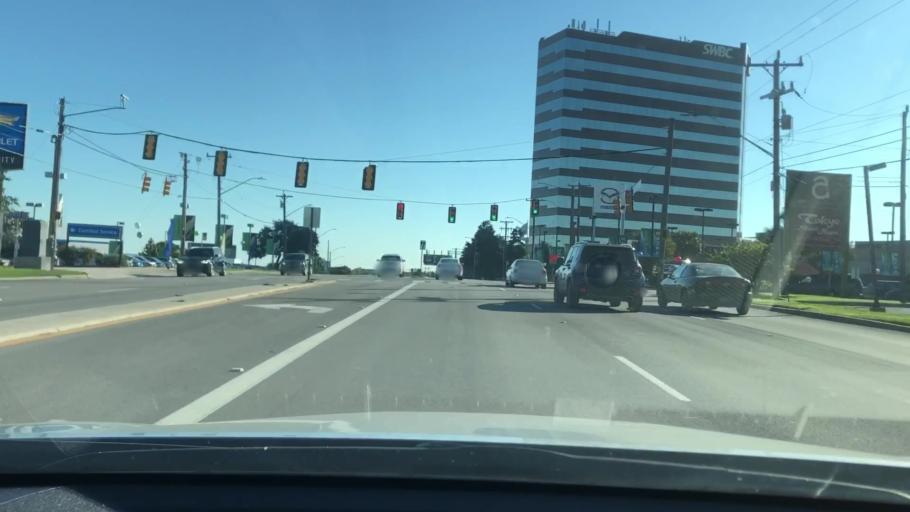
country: US
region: Texas
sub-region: Bexar County
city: Castle Hills
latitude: 29.5270
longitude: -98.4985
